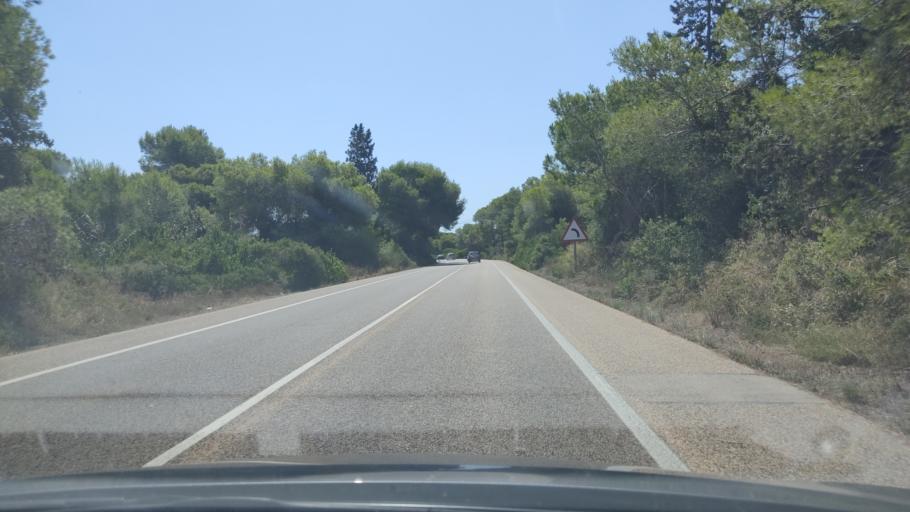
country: ES
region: Valencia
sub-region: Provincia de Valencia
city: Sollana
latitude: 39.3169
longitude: -0.3052
